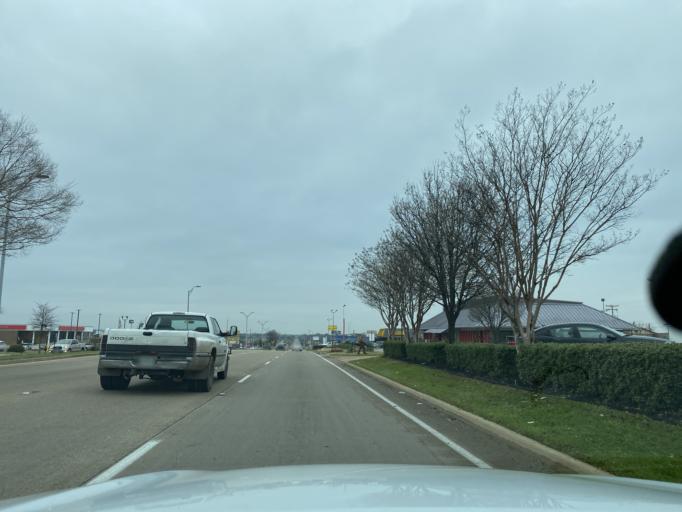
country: US
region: Texas
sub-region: Tarrant County
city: Arlington
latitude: 32.7082
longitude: -97.0929
